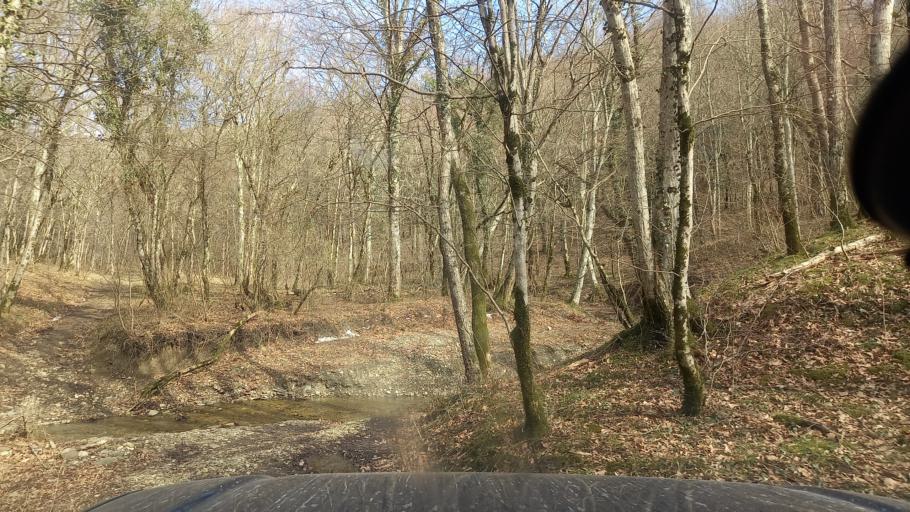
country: RU
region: Krasnodarskiy
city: Arkhipo-Osipovka
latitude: 44.3803
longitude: 38.5987
